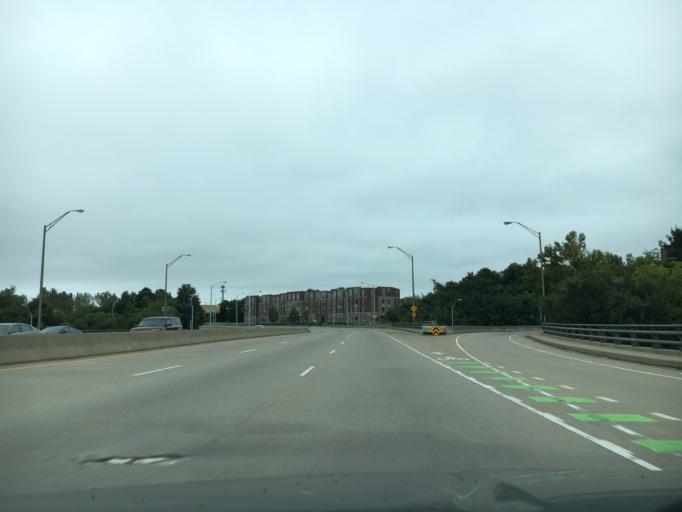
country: US
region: Virginia
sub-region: City of Richmond
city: Richmond
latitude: 37.5268
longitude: -77.4521
